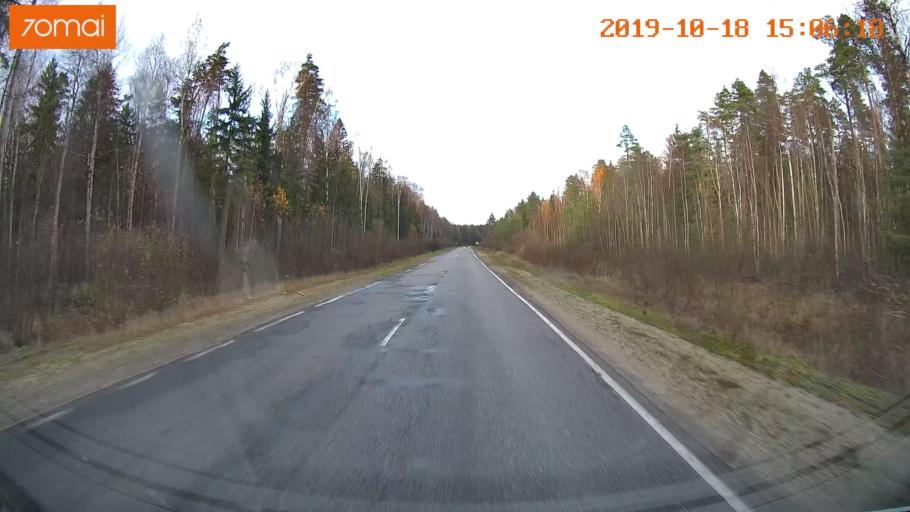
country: RU
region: Vladimir
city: Gus'-Khrustal'nyy
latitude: 55.5281
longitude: 40.5777
